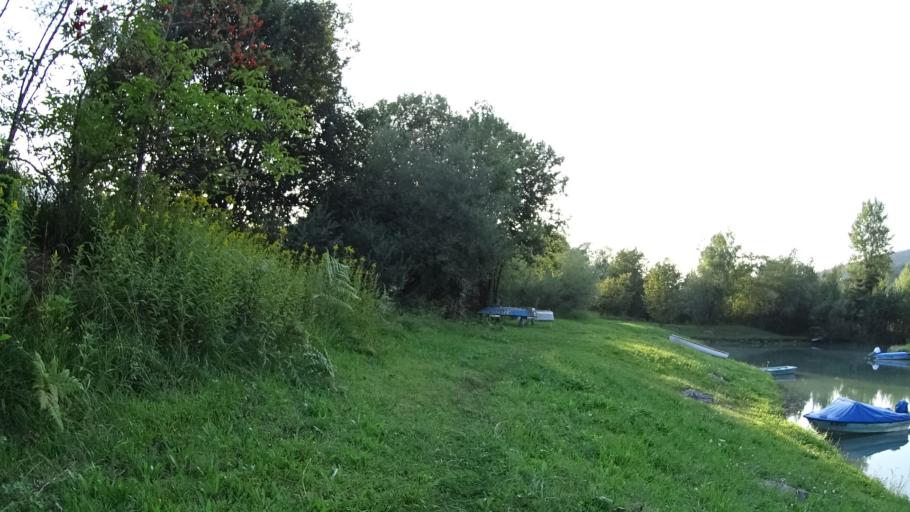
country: AT
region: Carinthia
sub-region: Politischer Bezirk Klagenfurt Land
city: Ludmannsdorf
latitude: 46.5370
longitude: 14.1105
